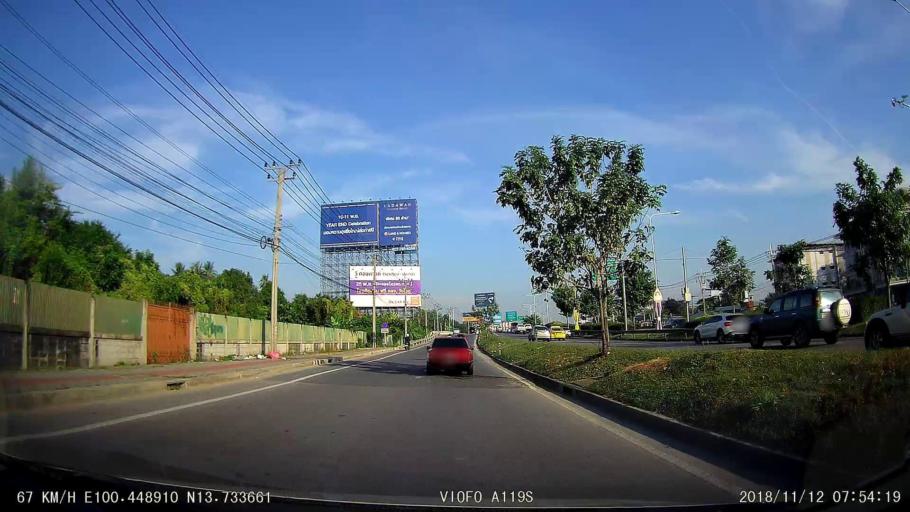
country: TH
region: Bangkok
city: Phasi Charoen
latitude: 13.7339
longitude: 100.4488
